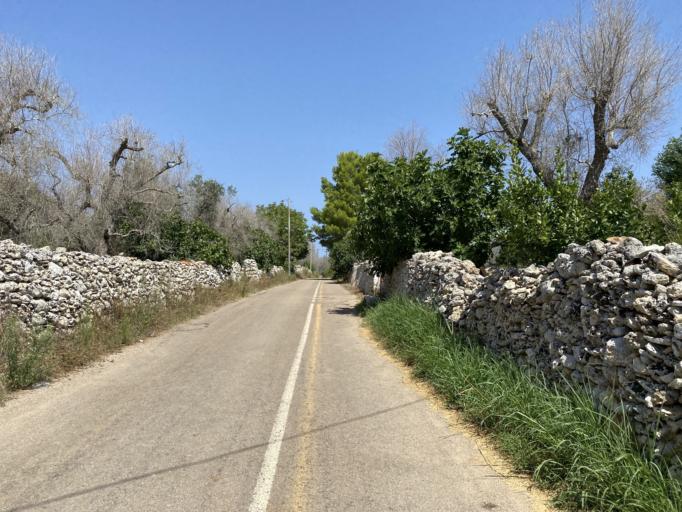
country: IT
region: Apulia
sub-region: Provincia di Lecce
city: Sanarica
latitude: 40.0963
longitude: 18.3537
